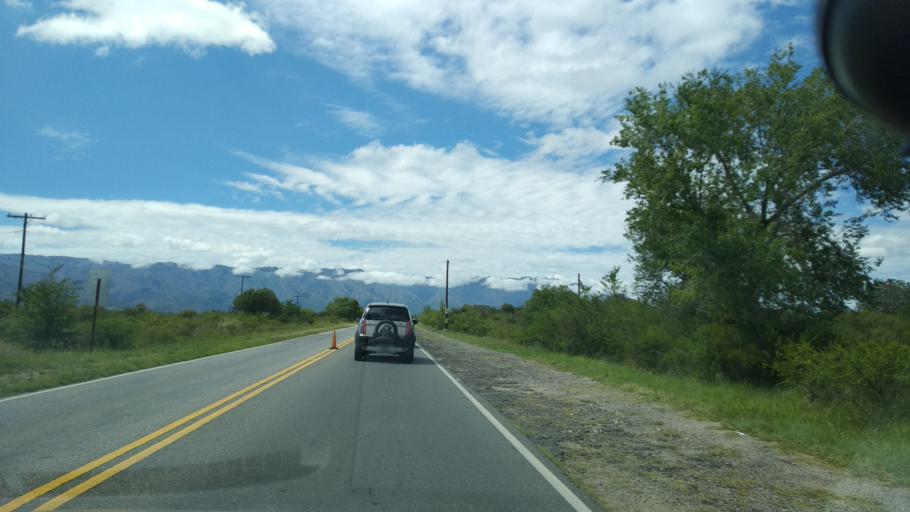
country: AR
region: Cordoba
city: Mina Clavero
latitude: -31.7517
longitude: -64.9774
